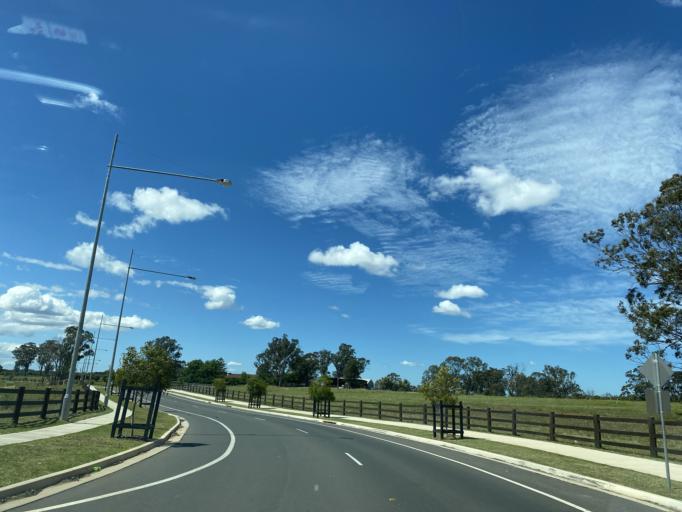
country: AU
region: New South Wales
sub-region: Campbelltown Municipality
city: Leumeah
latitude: -34.0123
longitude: 150.7914
